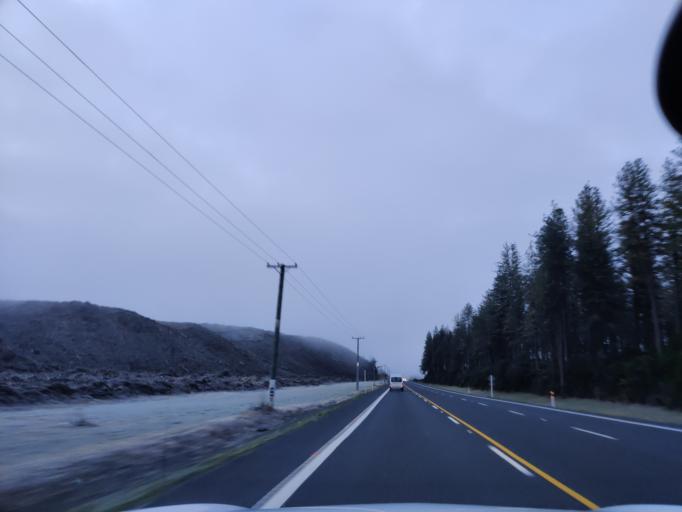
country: NZ
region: Waikato
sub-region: South Waikato District
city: Tokoroa
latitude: -38.3830
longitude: 176.0047
